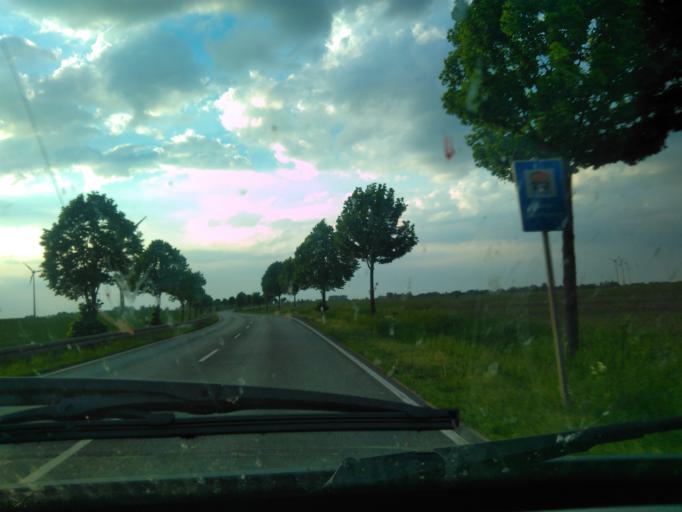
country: DE
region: Saxony-Anhalt
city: Stossen
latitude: 51.1010
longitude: 11.9382
